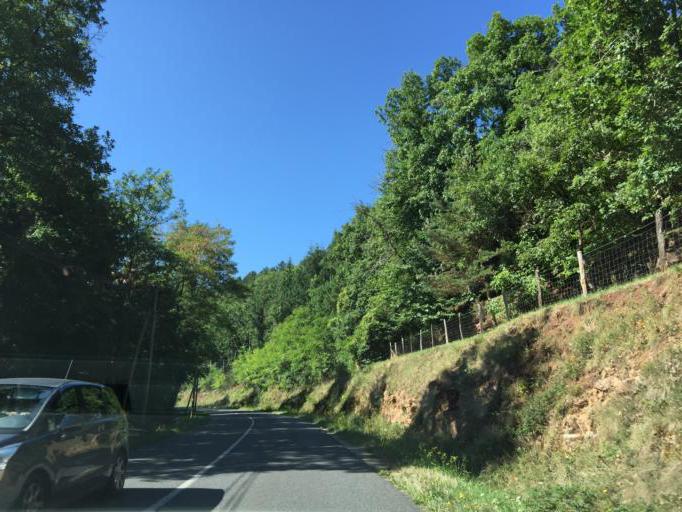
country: FR
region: Midi-Pyrenees
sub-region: Departement de l'Aveyron
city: Saint-Georges-de-Luzencon
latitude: 44.0994
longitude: 2.9005
